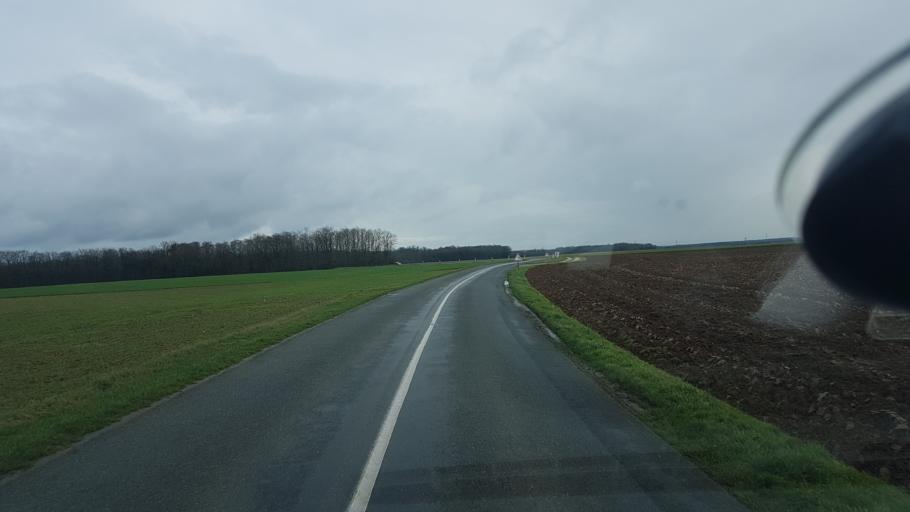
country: FR
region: Ile-de-France
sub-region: Departement de Seine-et-Marne
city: Souppes-sur-Loing
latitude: 48.2273
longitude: 2.8022
